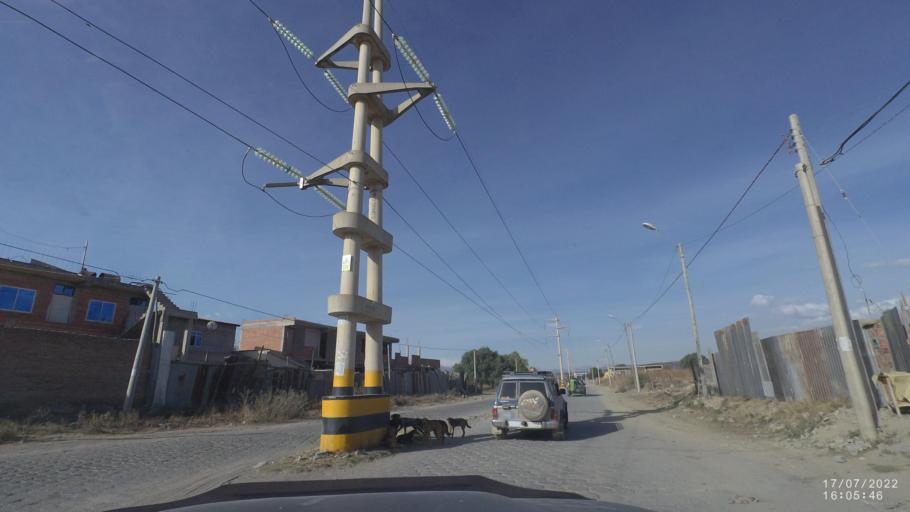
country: BO
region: Cochabamba
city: Sipe Sipe
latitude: -17.4150
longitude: -66.2814
